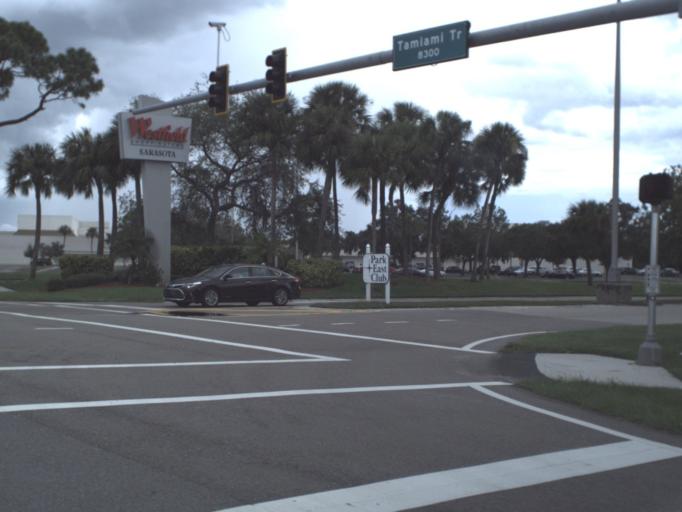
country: US
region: Florida
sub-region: Sarasota County
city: Vamo
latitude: 27.2304
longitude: -82.4950
